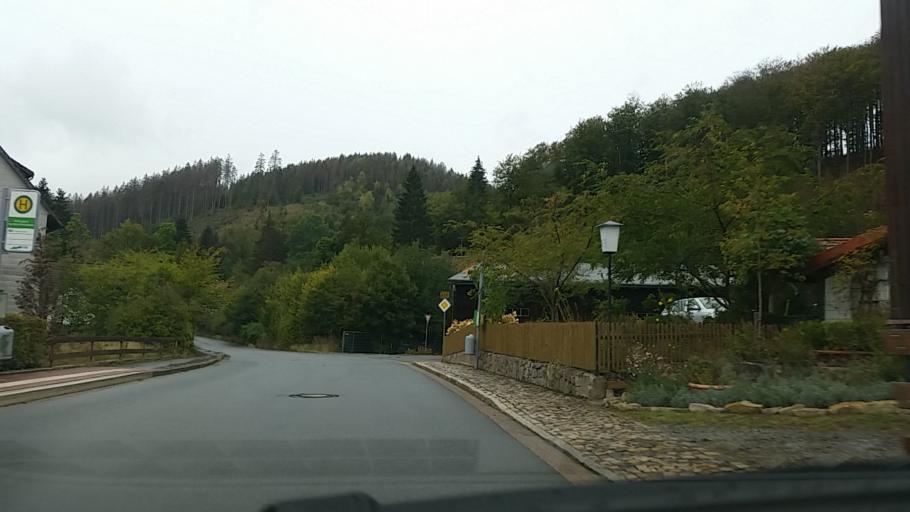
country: DE
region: Lower Saxony
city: Clausthal-Zellerfeld
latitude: 51.7529
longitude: 10.3769
